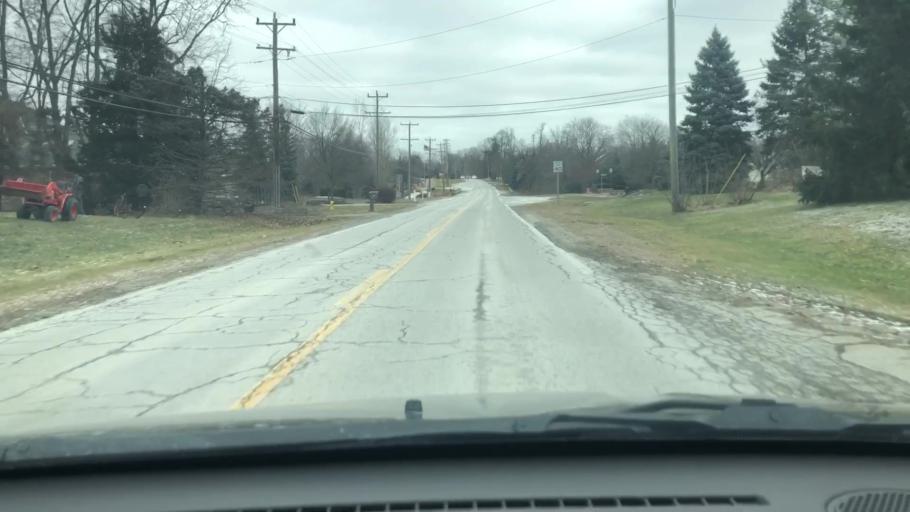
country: US
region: Michigan
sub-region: Macomb County
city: Shelby
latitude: 42.7236
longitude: -83.0518
